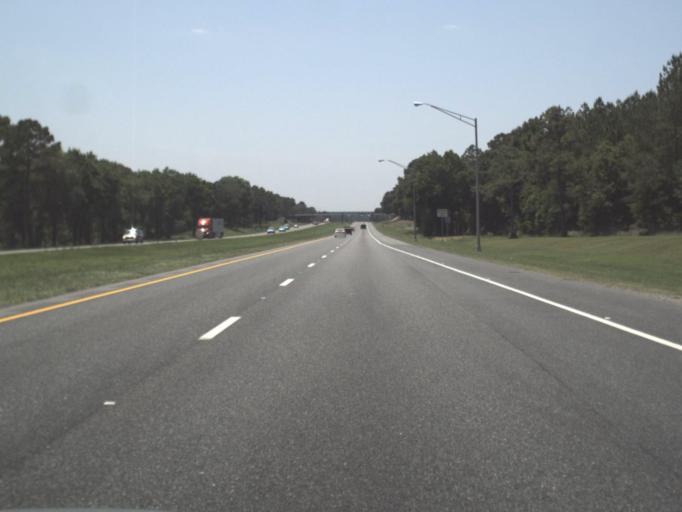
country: US
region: Florida
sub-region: Suwannee County
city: Wellborn
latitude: 30.2733
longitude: -82.7874
